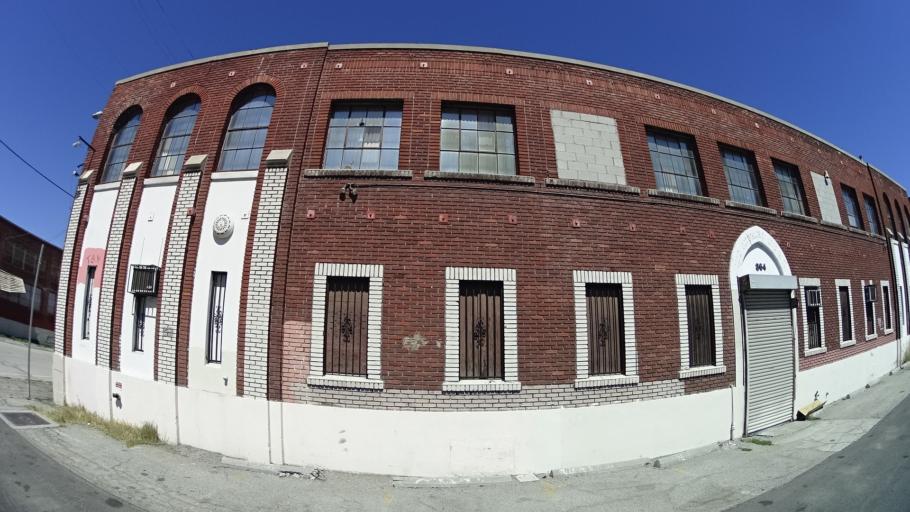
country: US
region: California
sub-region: Los Angeles County
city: Los Angeles
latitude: 34.0429
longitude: -118.2258
